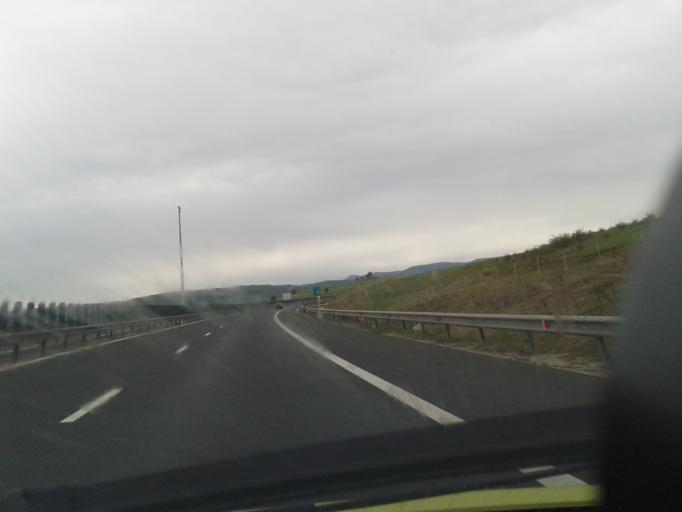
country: RO
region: Sibiu
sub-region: Comuna Apoldu de Jos
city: Apoldu de Jos
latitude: 45.8677
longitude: 23.8792
